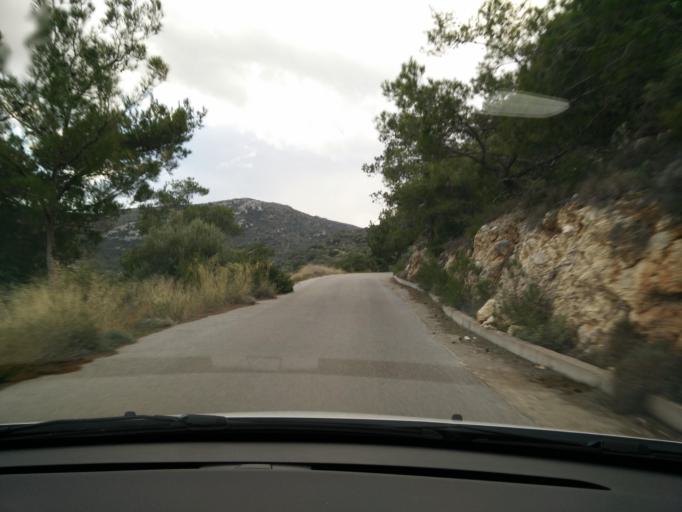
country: GR
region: Crete
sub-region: Nomos Lasithiou
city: Kritsa
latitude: 35.0995
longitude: 25.6925
